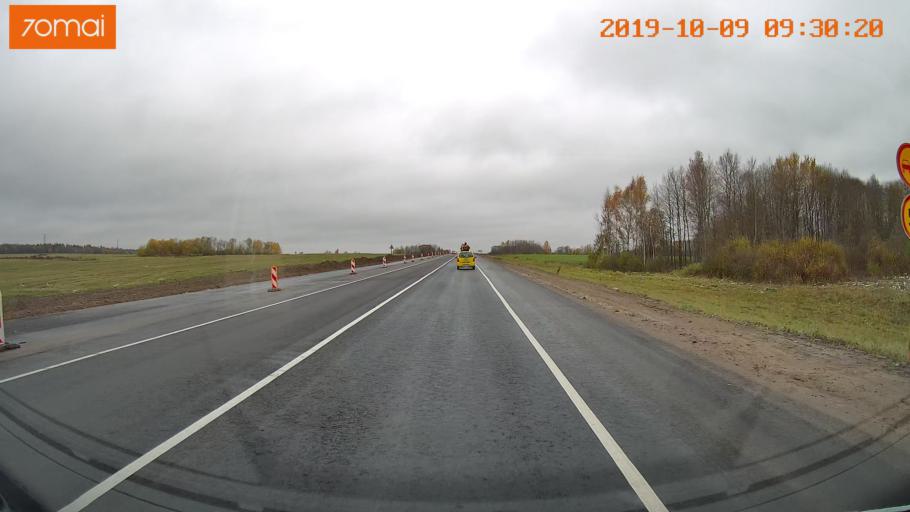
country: RU
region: Vologda
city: Vologda
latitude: 59.1390
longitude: 39.9500
